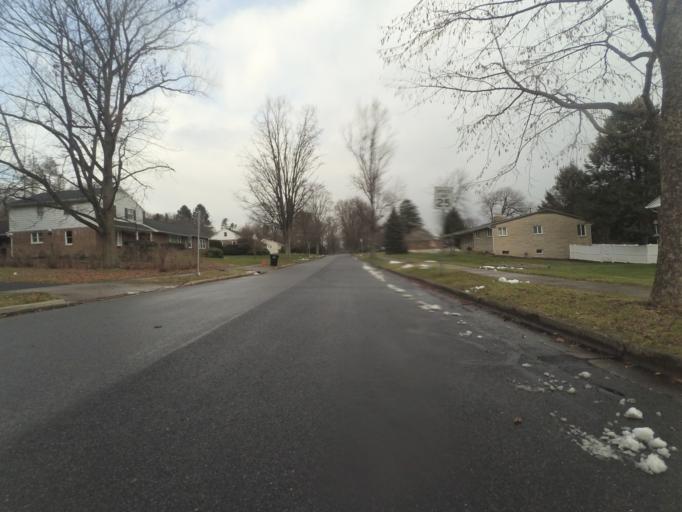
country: US
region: Pennsylvania
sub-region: Centre County
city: State College
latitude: 40.7937
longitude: -77.8479
